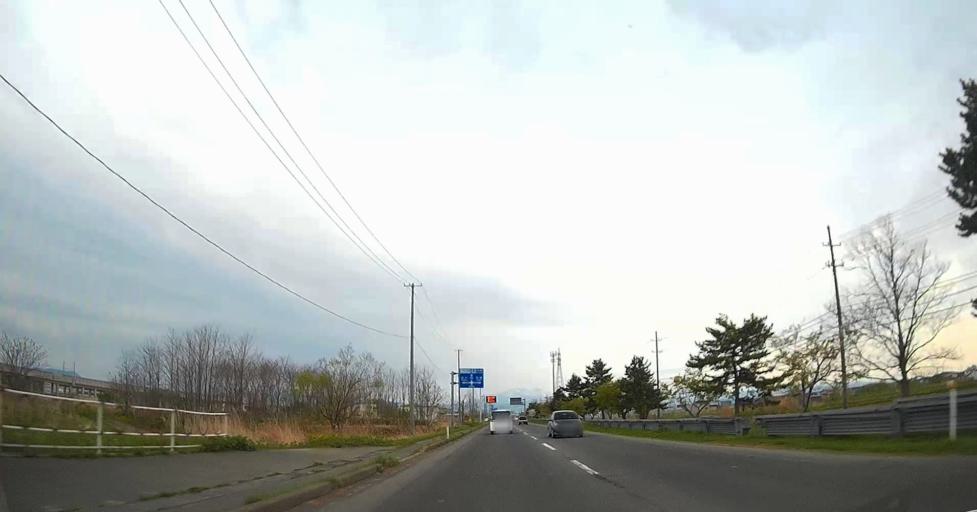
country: JP
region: Aomori
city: Aomori Shi
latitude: 40.8460
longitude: 140.6846
